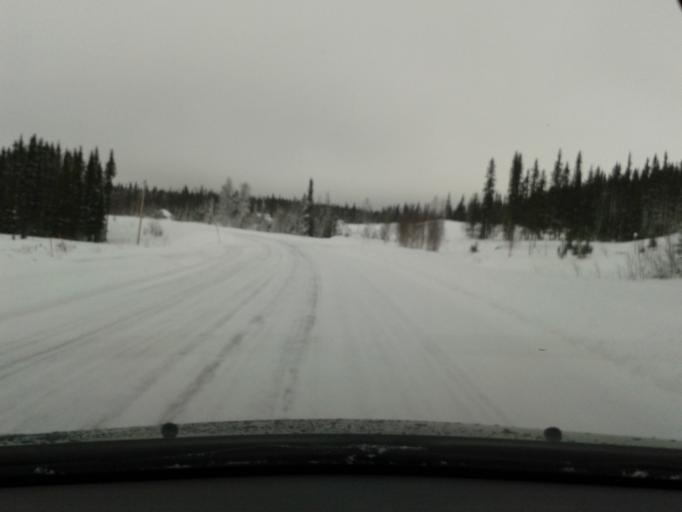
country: SE
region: Vaesterbotten
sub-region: Vilhelmina Kommun
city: Sjoberg
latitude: 65.1834
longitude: 15.8965
